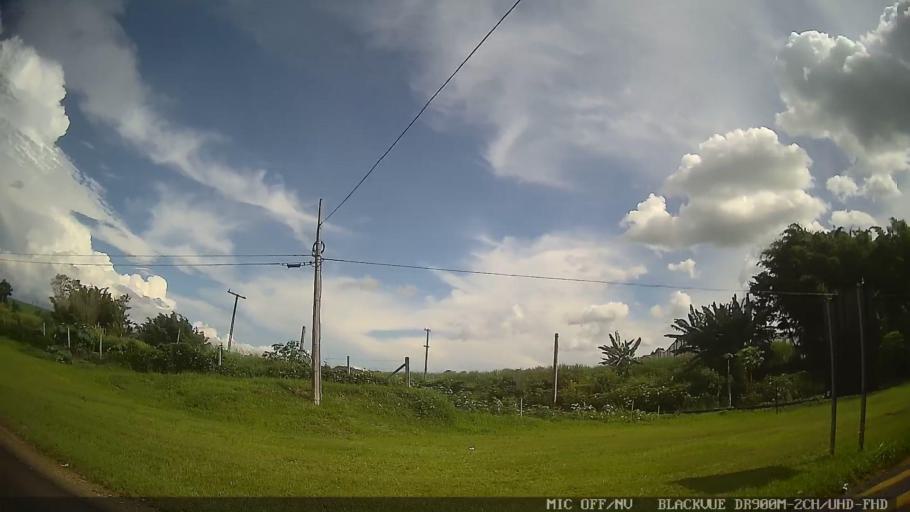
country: BR
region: Sao Paulo
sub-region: Laranjal Paulista
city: Laranjal Paulista
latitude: -23.0410
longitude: -47.9038
